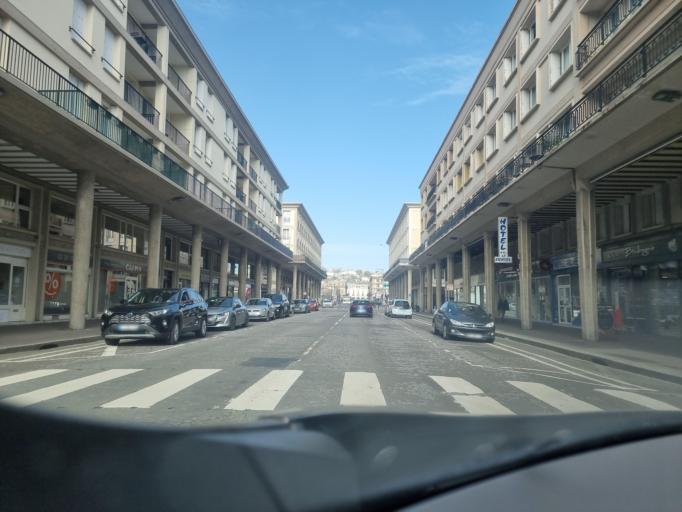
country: FR
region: Haute-Normandie
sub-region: Departement de la Seine-Maritime
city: Le Havre
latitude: 49.4885
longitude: 0.1075
